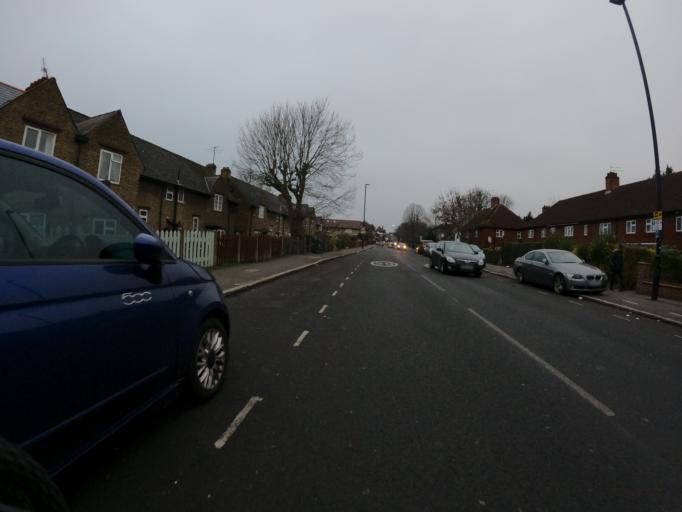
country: GB
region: England
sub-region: Greater London
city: Brentford
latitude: 51.4935
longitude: -0.3049
